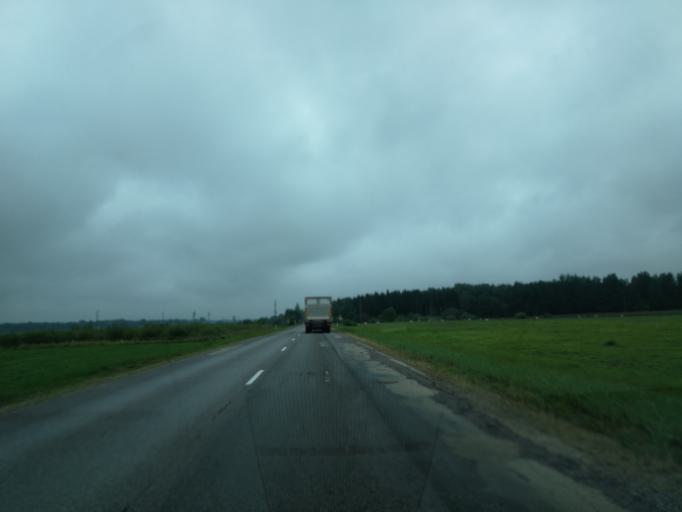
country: LV
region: Livani
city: Livani
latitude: 56.3485
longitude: 26.2720
